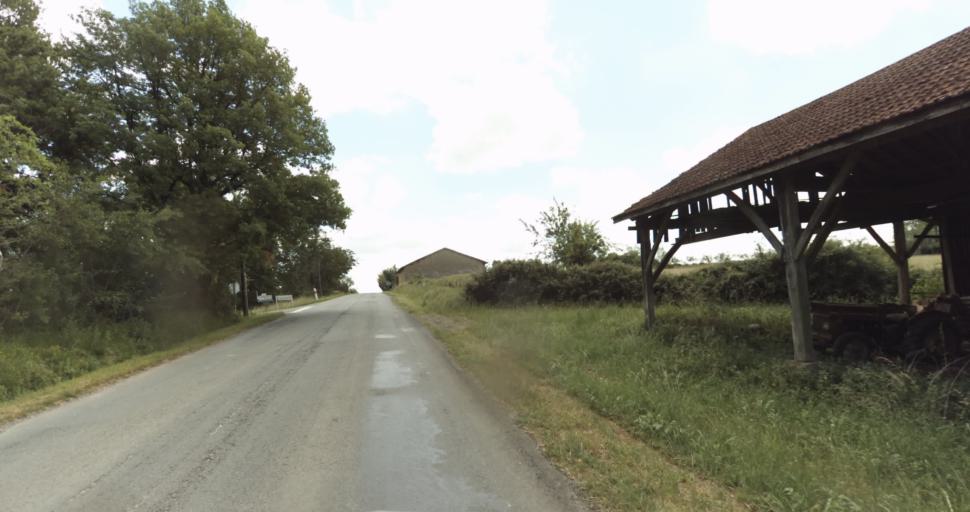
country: FR
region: Aquitaine
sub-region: Departement de la Dordogne
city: Beaumont-du-Perigord
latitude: 44.7281
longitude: 0.7907
